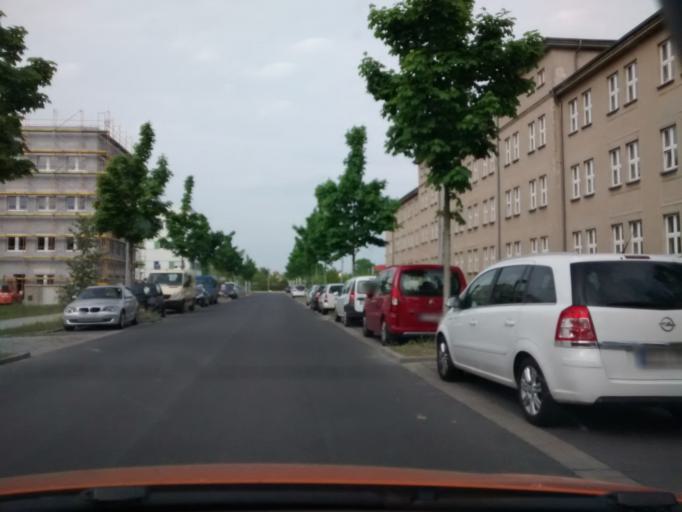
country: DE
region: Berlin
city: Adlershof
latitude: 52.4357
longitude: 13.5335
